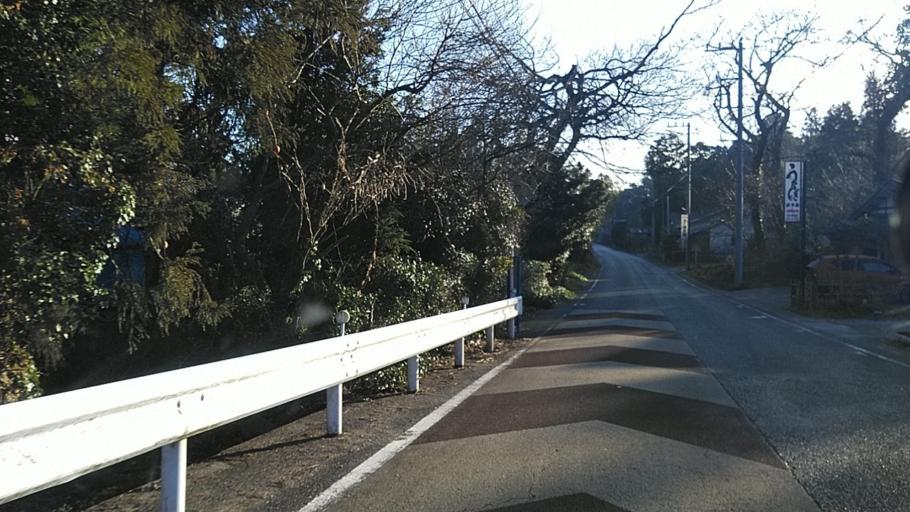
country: JP
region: Chiba
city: Kimitsu
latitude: 35.2542
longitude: 139.9653
